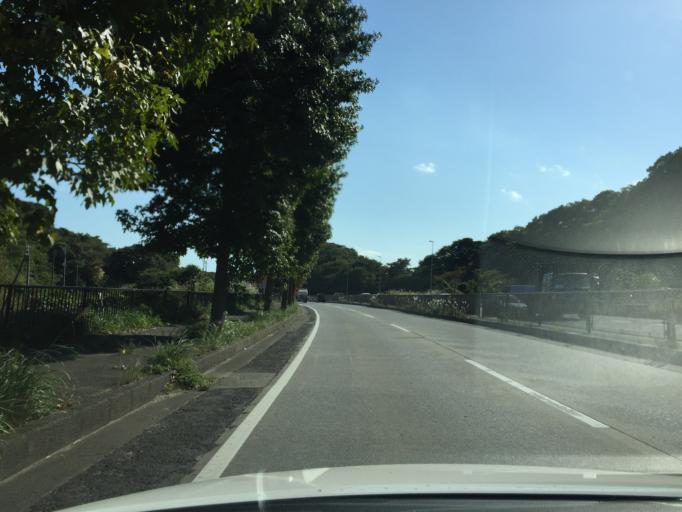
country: JP
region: Fukushima
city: Iwaki
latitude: 36.9993
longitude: 140.8975
